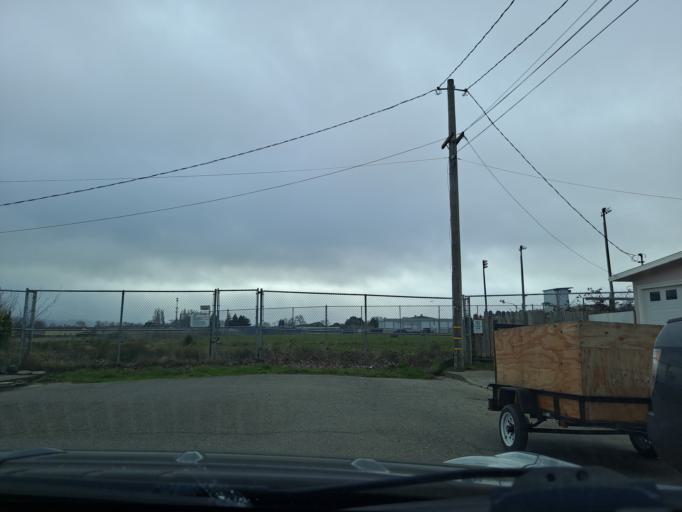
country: US
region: California
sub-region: Humboldt County
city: Fortuna
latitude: 40.5936
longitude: -124.1496
